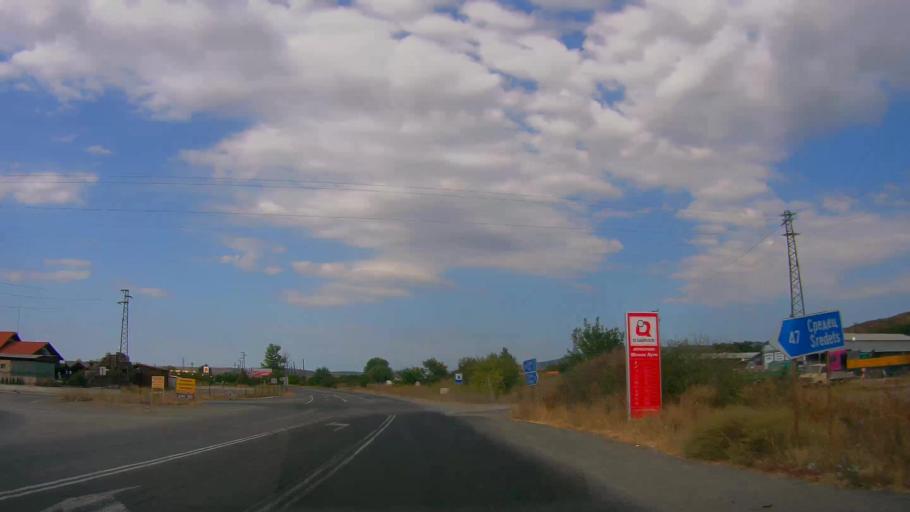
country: BG
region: Burgas
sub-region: Obshtina Aytos
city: Aytos
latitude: 42.7053
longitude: 27.2370
